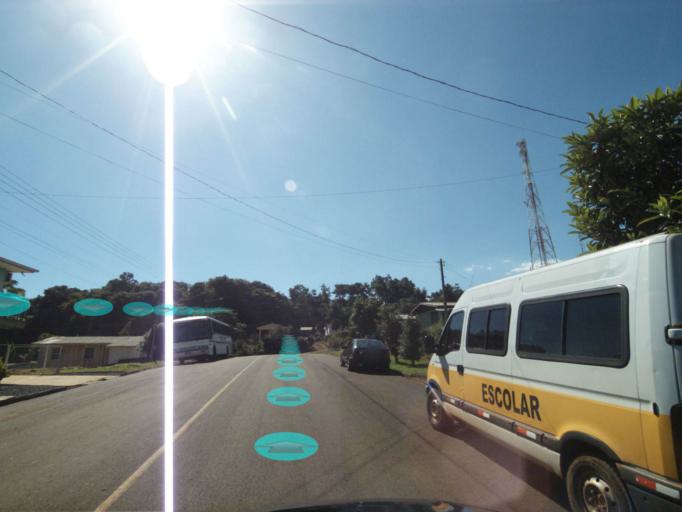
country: BR
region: Parana
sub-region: Coronel Vivida
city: Coronel Vivida
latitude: -26.1434
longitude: -52.3887
